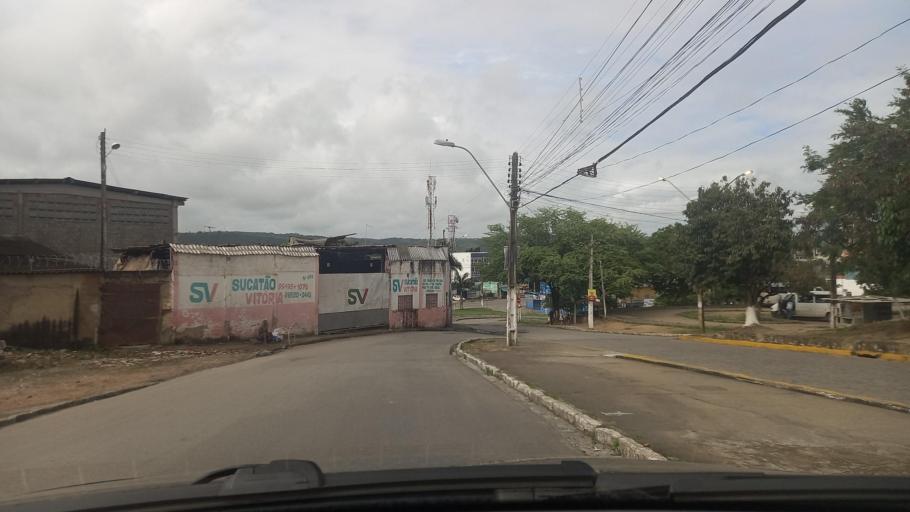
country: BR
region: Pernambuco
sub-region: Vitoria De Santo Antao
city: Vitoria de Santo Antao
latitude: -8.1143
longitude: -35.2963
